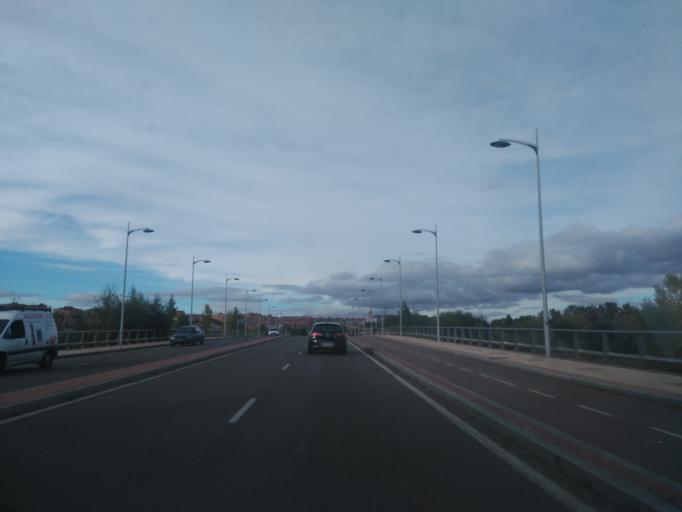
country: ES
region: Castille and Leon
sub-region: Provincia de Salamanca
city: Santa Marta de Tormes
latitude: 40.9590
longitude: -5.6450
